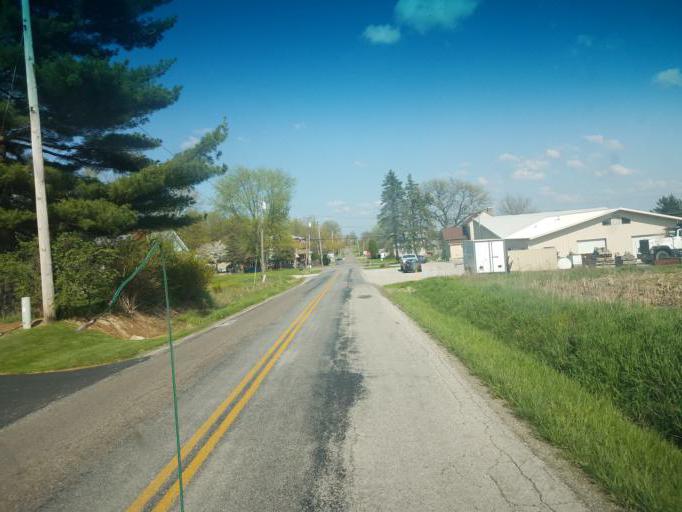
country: US
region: Ohio
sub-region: Wayne County
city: Smithville
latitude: 40.8796
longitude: -81.9210
